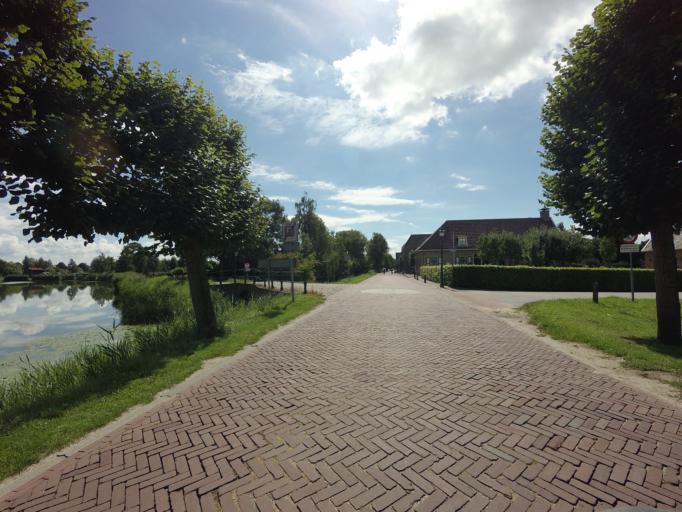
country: NL
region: South Holland
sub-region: Gemeente Schoonhoven
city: Schoonhoven
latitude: 51.9330
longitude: 4.8698
